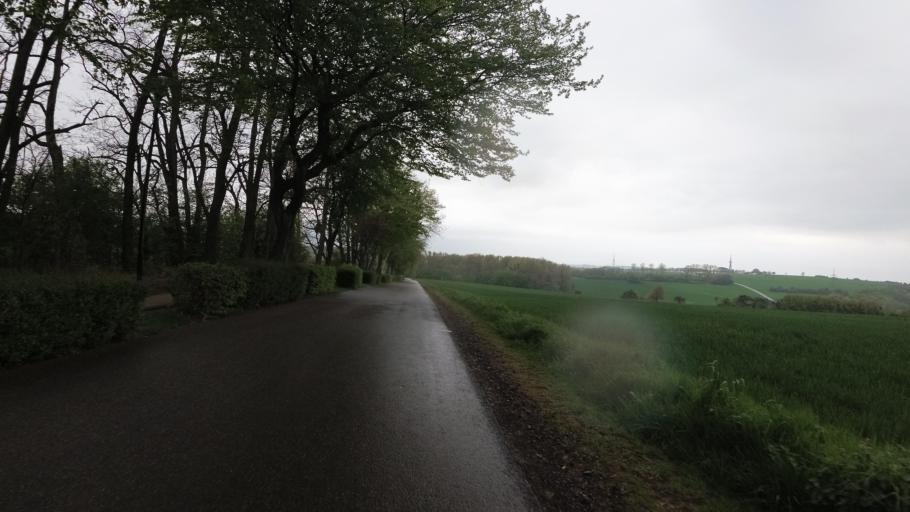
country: FR
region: Lorraine
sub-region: Departement de la Moselle
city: Merten
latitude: 49.2691
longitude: 6.6802
